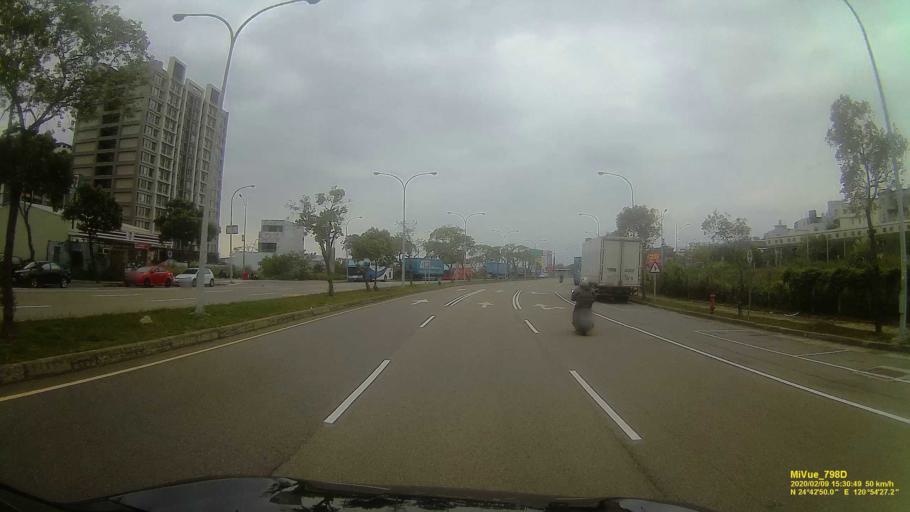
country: TW
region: Taiwan
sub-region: Hsinchu
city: Hsinchu
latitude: 24.7138
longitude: 120.9073
